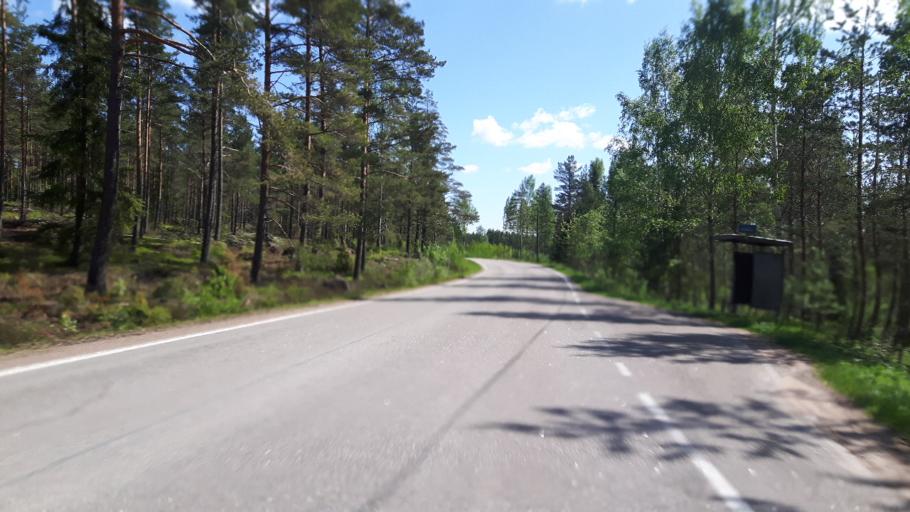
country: FI
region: Kymenlaakso
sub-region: Kotka-Hamina
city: Hamina
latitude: 60.5138
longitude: 27.4212
